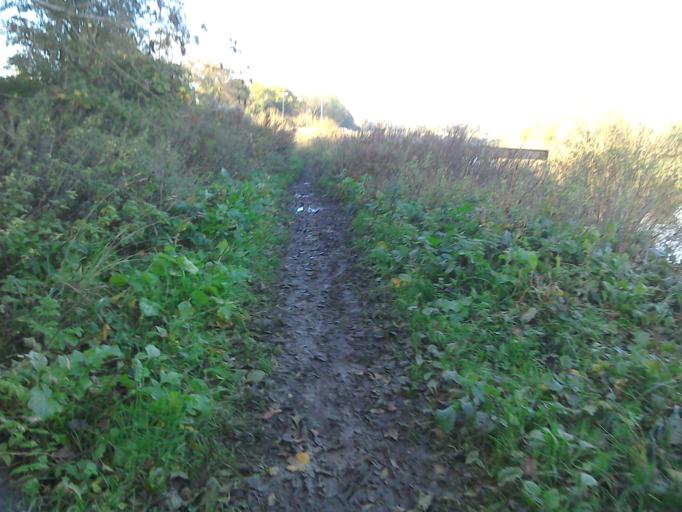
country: GB
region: England
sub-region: Oxfordshire
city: Radley
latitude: 51.7022
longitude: -1.2327
